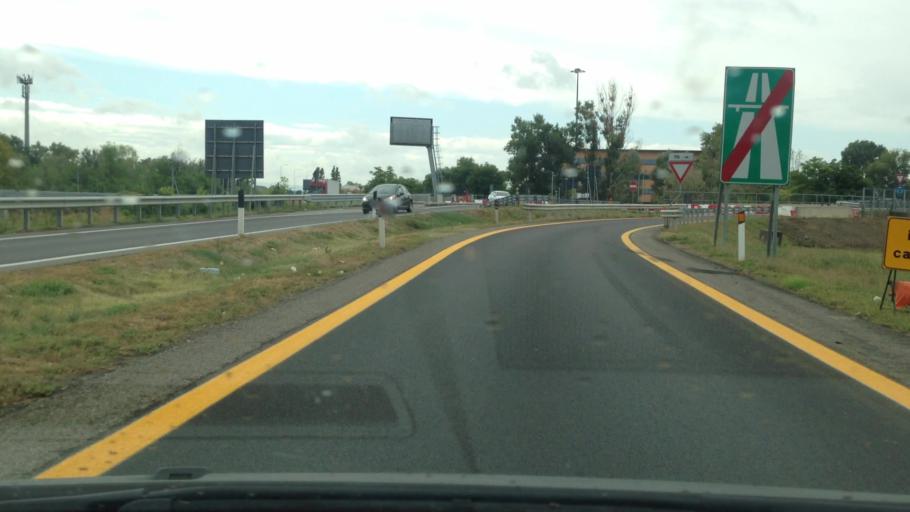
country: IT
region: Piedmont
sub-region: Provincia di Alessandria
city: Tortona
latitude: 44.9088
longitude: 8.8371
